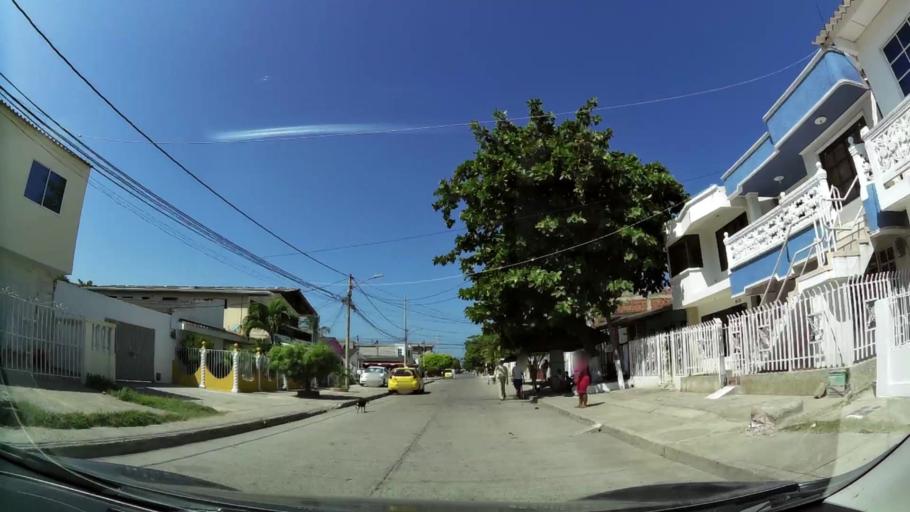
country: CO
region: Bolivar
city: Cartagena
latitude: 10.4412
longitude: -75.5209
